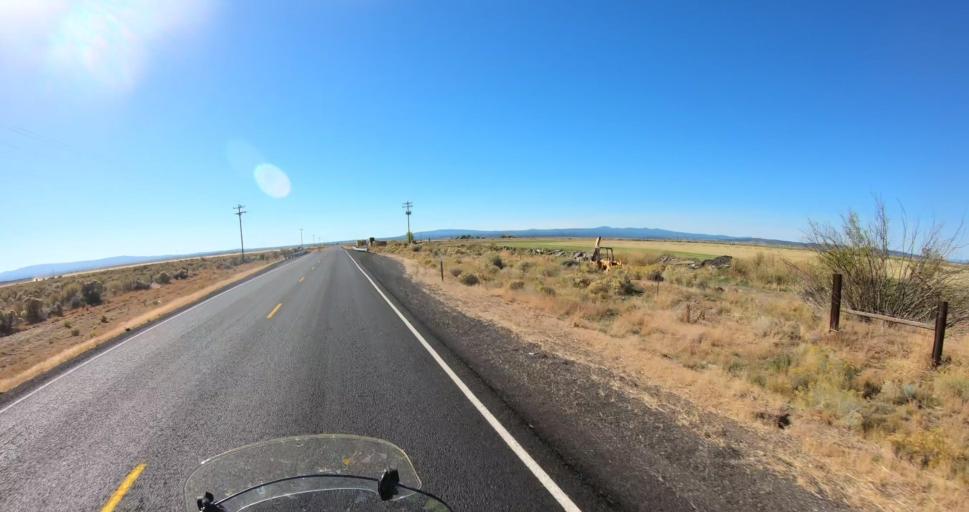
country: US
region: Oregon
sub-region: Deschutes County
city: La Pine
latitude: 43.1280
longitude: -120.9818
